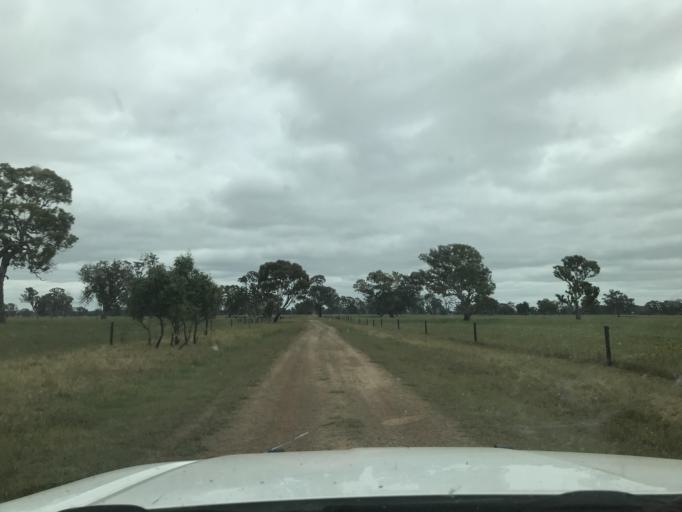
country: AU
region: South Australia
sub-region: Wattle Range
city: Penola
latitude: -37.1774
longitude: 141.0428
